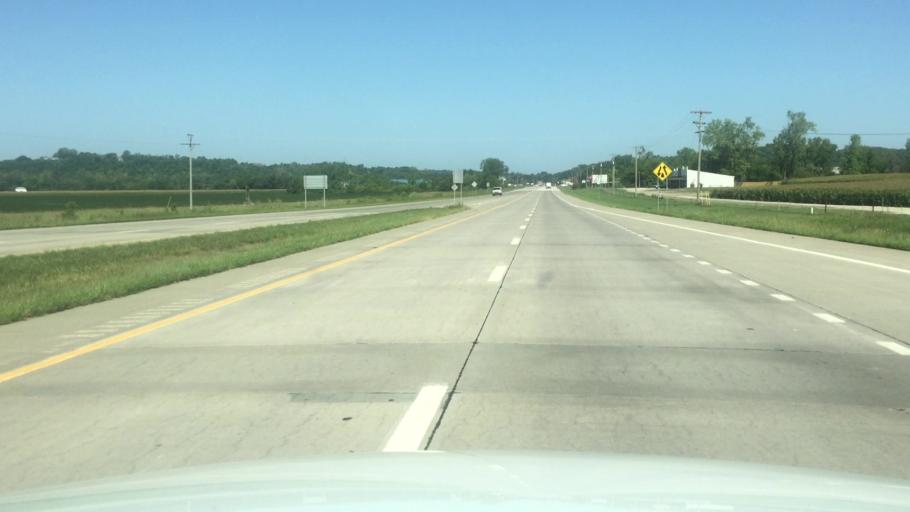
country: US
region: Kansas
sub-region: Doniphan County
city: Wathena
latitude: 39.7502
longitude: -94.9290
